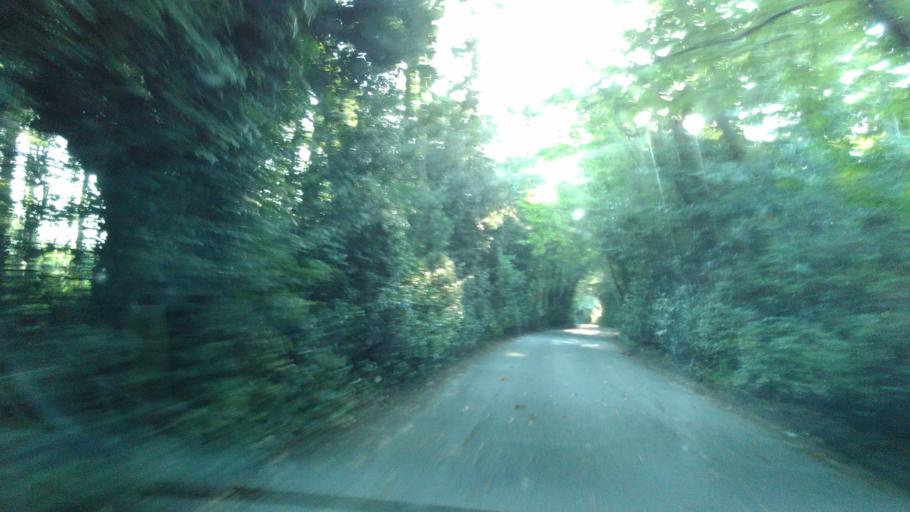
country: GB
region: England
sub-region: Kent
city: Chartham
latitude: 51.2732
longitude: 1.0185
